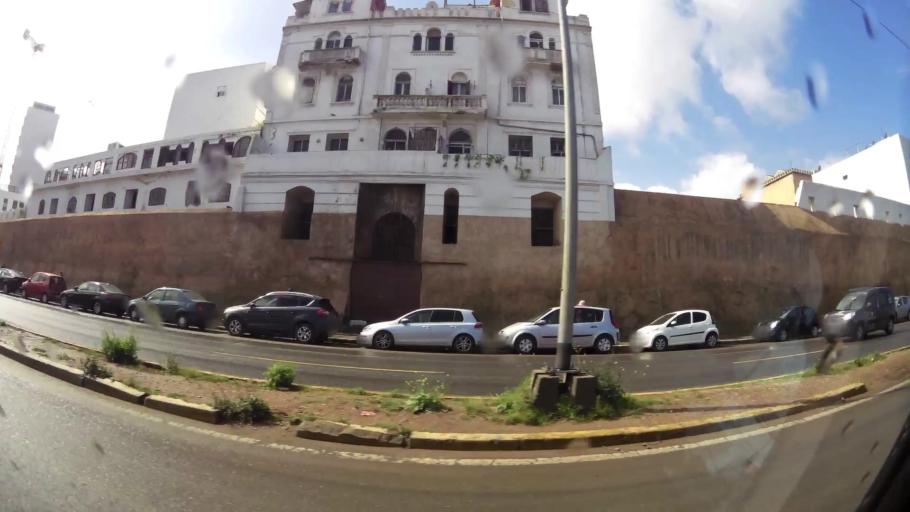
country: MA
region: Grand Casablanca
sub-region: Casablanca
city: Casablanca
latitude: 33.6005
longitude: -7.6156
